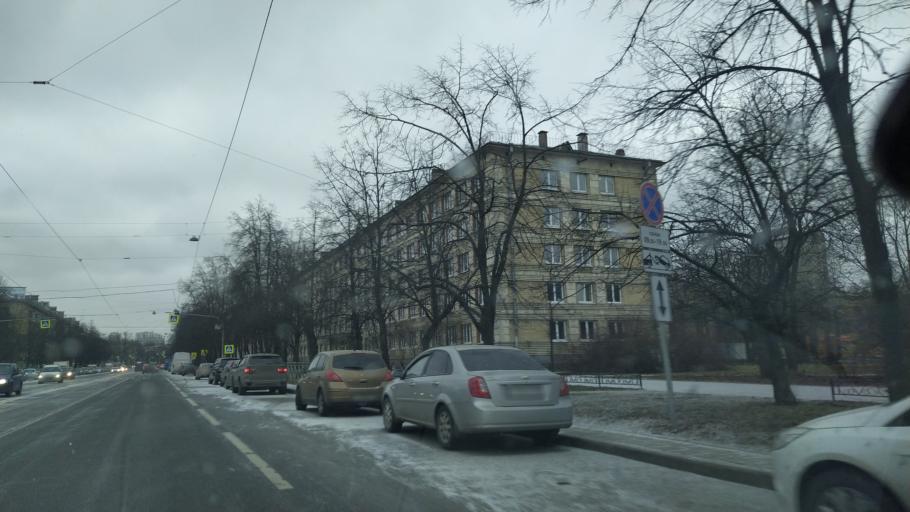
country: RU
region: St.-Petersburg
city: Kupchino
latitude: 59.8477
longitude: 30.3300
